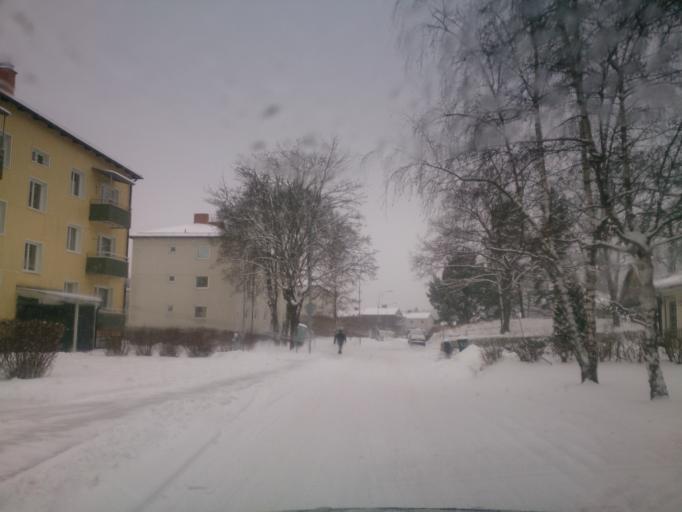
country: SE
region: OEstergoetland
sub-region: Finspangs Kommun
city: Finspang
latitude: 58.7087
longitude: 15.7898
